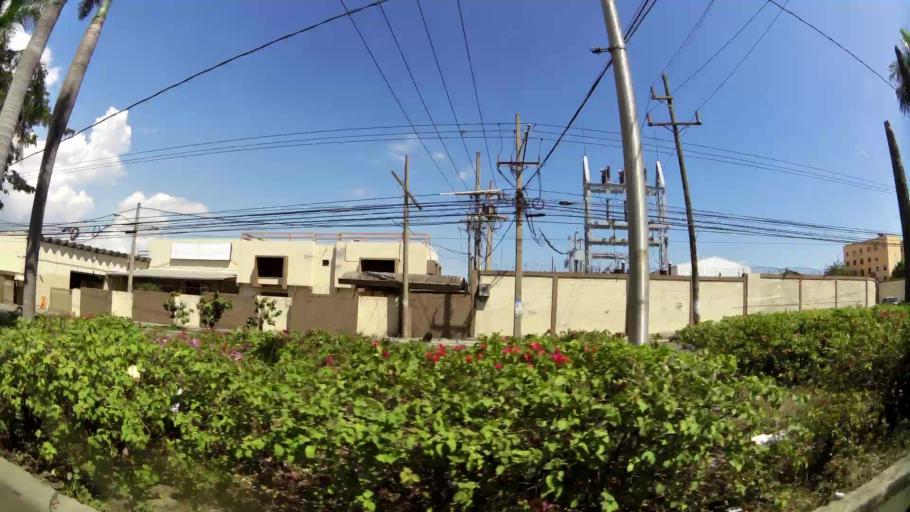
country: DO
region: Santo Domingo
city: Santo Domingo Oeste
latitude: 18.4671
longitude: -69.9948
